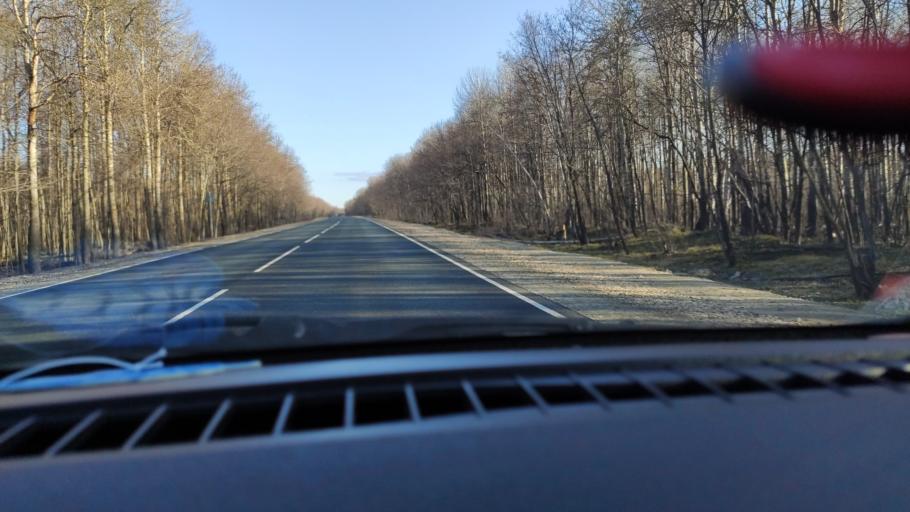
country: RU
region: Saratov
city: Khvalynsk
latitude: 52.4679
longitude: 48.0167
